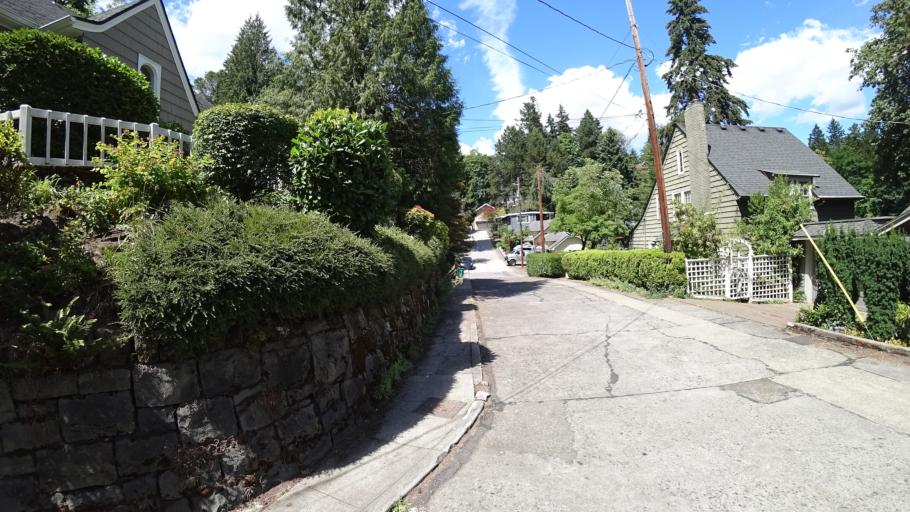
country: US
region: Oregon
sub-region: Multnomah County
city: Portland
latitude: 45.5052
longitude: -122.6963
